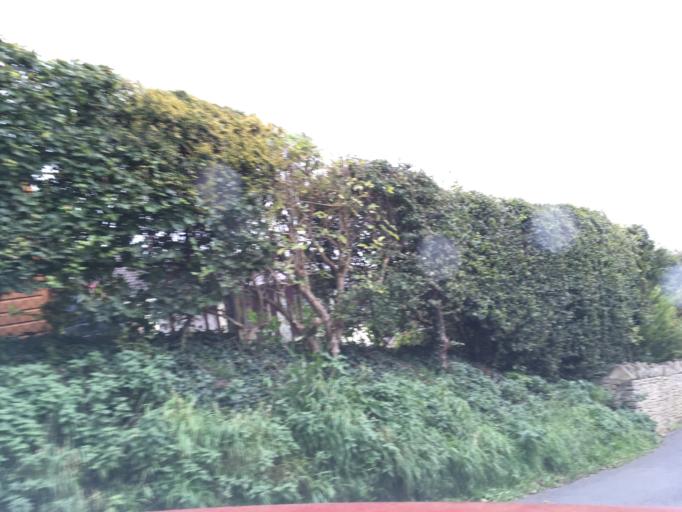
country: GB
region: England
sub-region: Gloucestershire
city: Stonehouse
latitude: 51.7518
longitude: -2.2544
